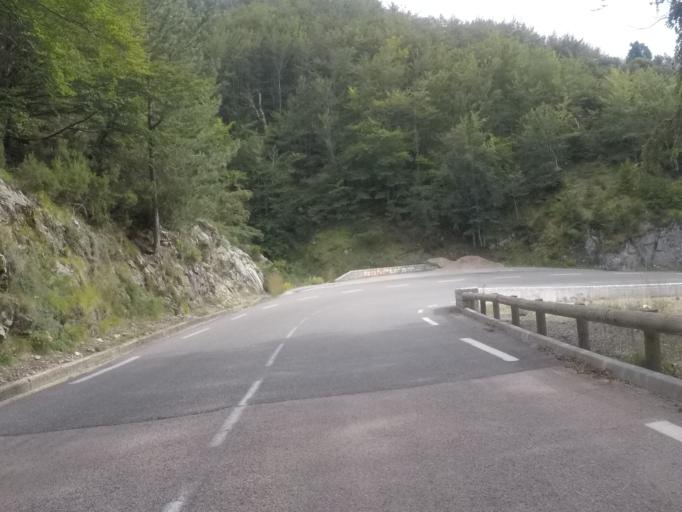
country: FR
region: Corsica
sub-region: Departement de la Haute-Corse
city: Corte
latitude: 42.1062
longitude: 9.1094
